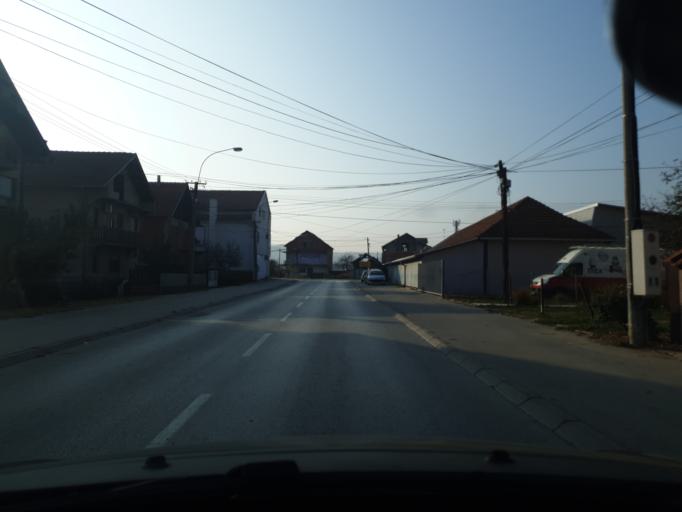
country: RS
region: Central Serbia
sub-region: Jablanicki Okrug
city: Leskovac
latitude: 42.9976
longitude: 21.9236
